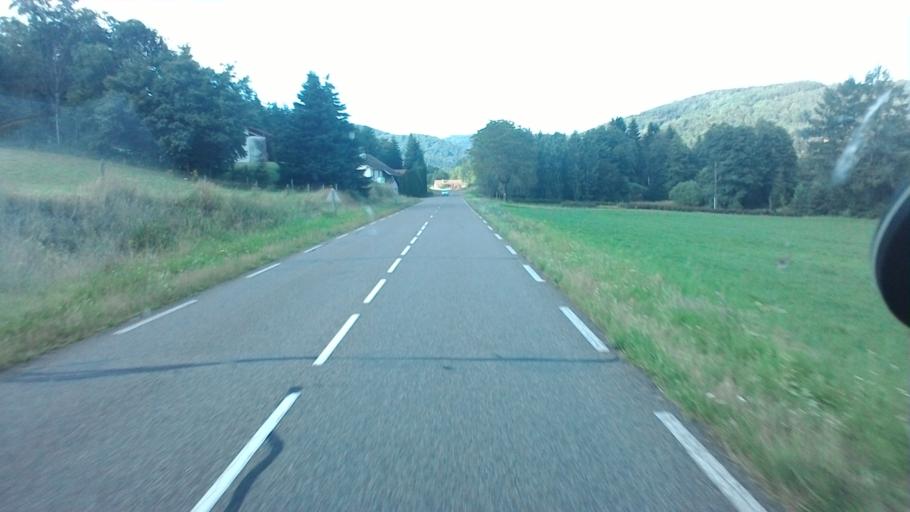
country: FR
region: Franche-Comte
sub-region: Departement de la Haute-Saone
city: Melisey
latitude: 47.8624
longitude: 6.5679
